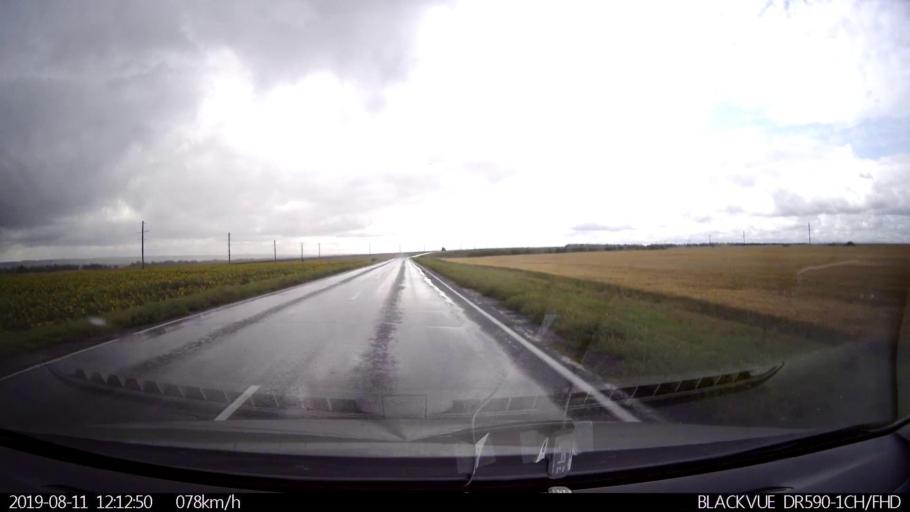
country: RU
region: Ulyanovsk
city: Silikatnyy
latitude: 53.9683
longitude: 47.9949
